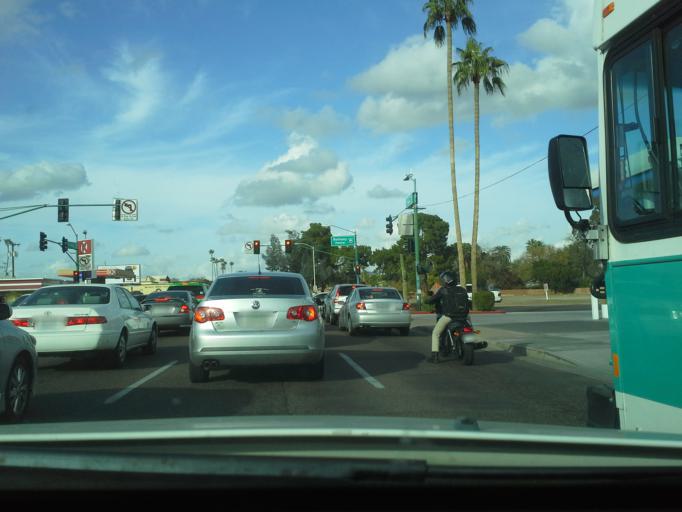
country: US
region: Arizona
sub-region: Maricopa County
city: Phoenix
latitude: 33.5233
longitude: -112.0824
